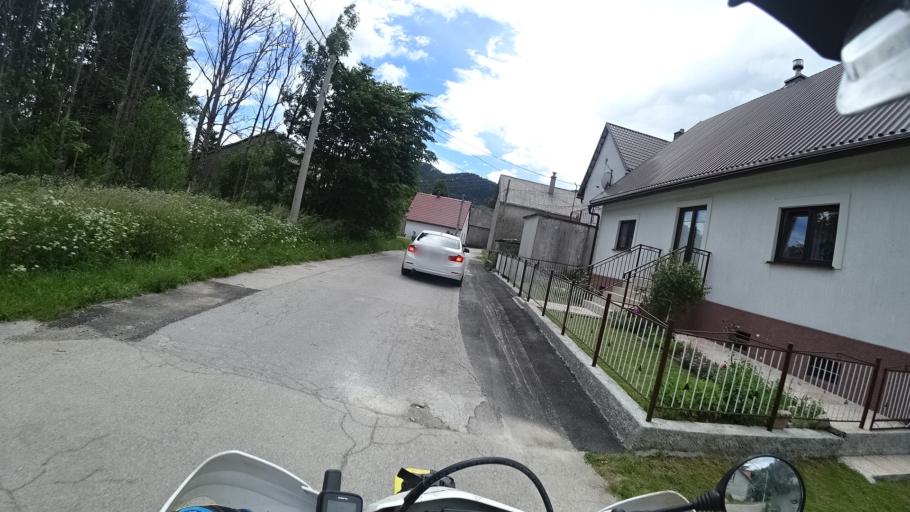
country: HR
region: Primorsko-Goranska
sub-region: Grad Crikvenica
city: Crikvenica
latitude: 45.2715
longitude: 14.7192
